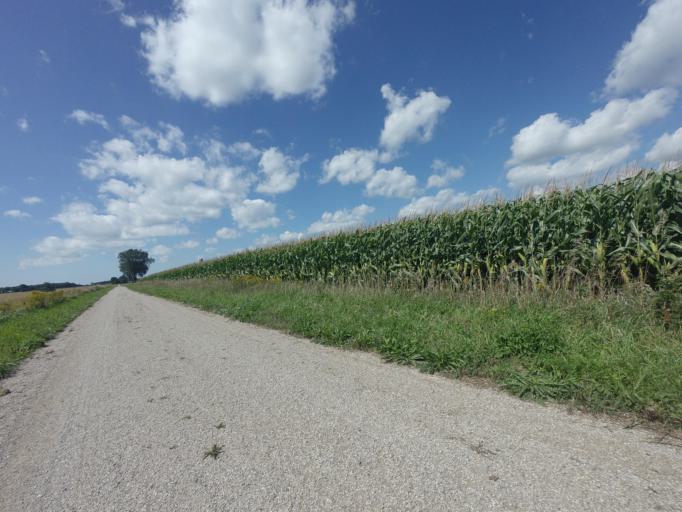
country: CA
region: Ontario
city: Huron East
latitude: 43.6633
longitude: -81.2584
